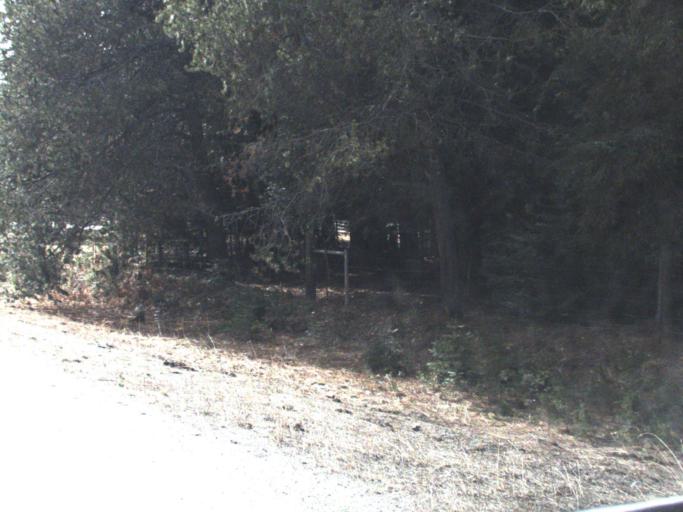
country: CA
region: British Columbia
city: Fruitvale
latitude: 48.6720
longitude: -117.3992
